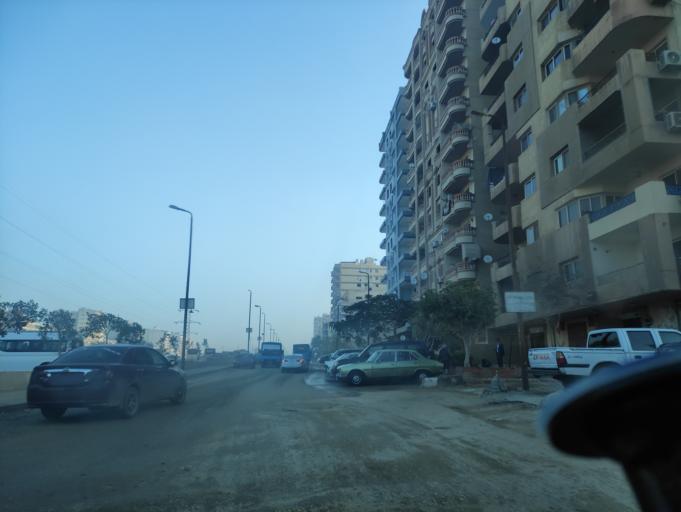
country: EG
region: Muhafazat al Qahirah
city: Cairo
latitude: 30.0491
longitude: 31.3681
